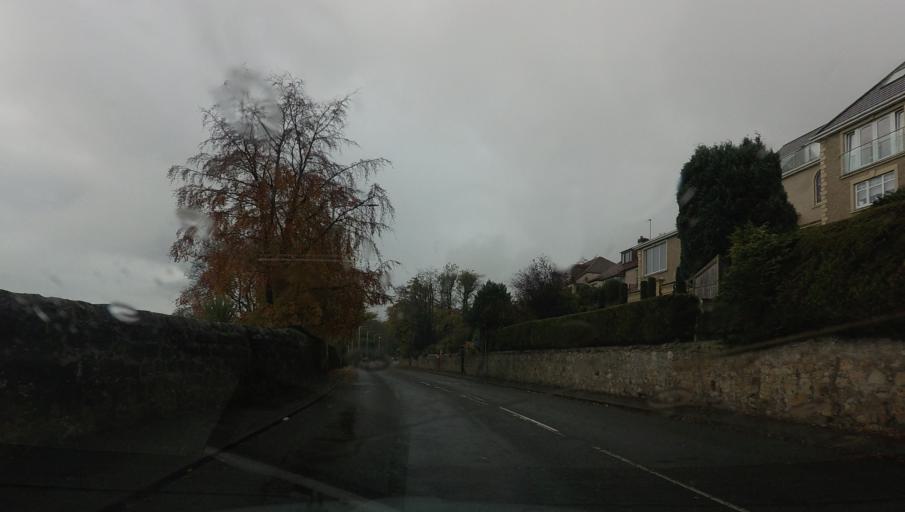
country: GB
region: Scotland
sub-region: Fife
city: Kirkcaldy
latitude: 56.1247
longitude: -3.1275
